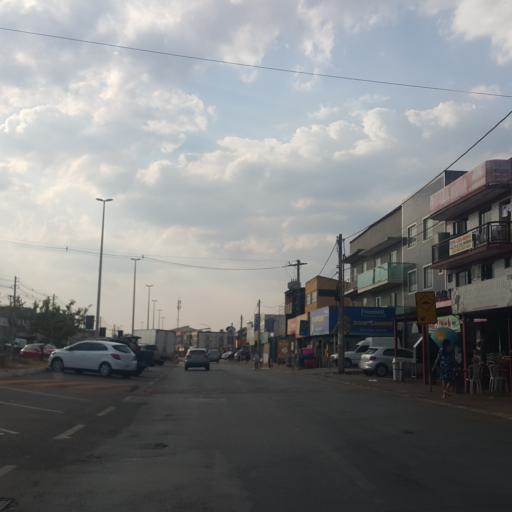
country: BR
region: Federal District
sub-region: Brasilia
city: Brasilia
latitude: -15.8648
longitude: -48.0240
